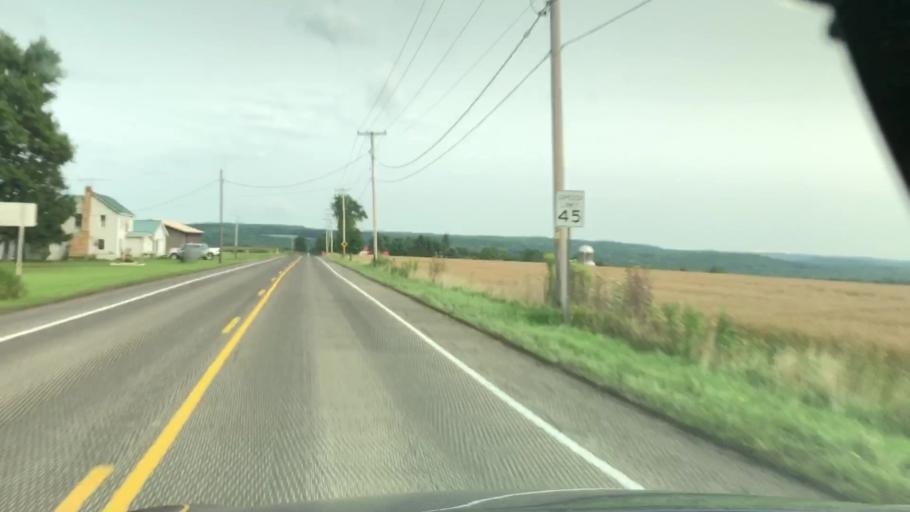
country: US
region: Pennsylvania
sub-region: Crawford County
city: Titusville
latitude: 41.7480
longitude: -79.7690
